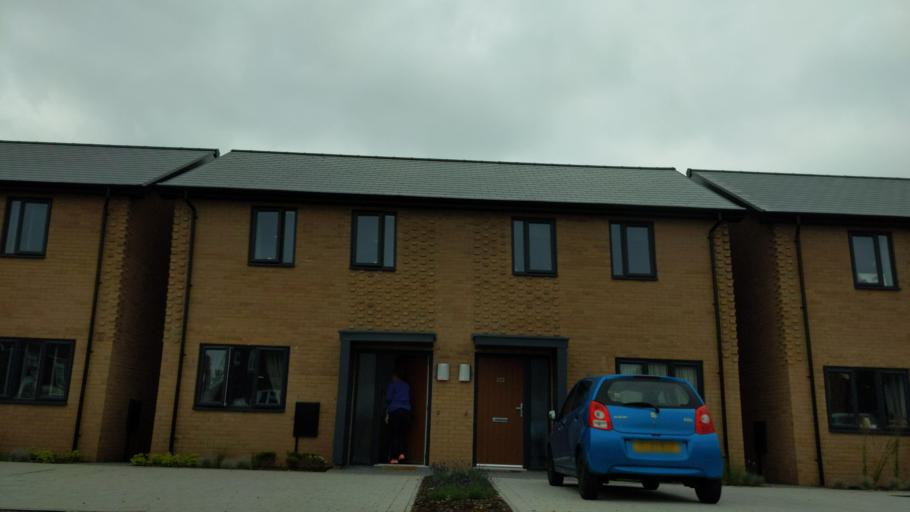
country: GB
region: England
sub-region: Worcestershire
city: Fernhill Heath
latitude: 52.2135
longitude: -2.1881
